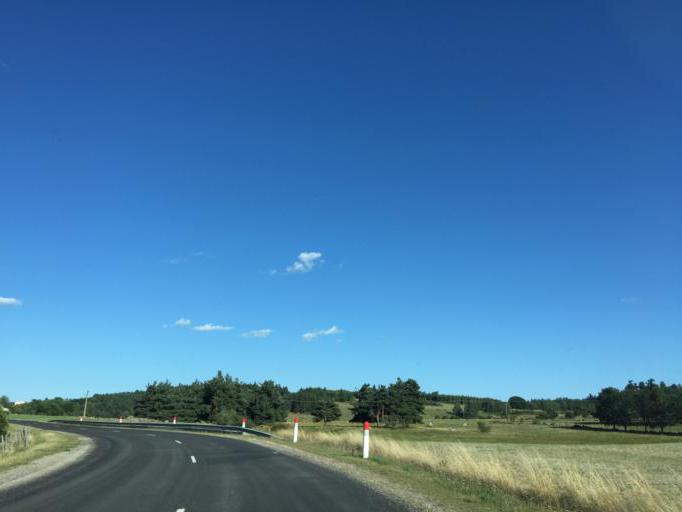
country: FR
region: Auvergne
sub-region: Departement de la Haute-Loire
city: Saugues
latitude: 44.9580
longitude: 3.5751
